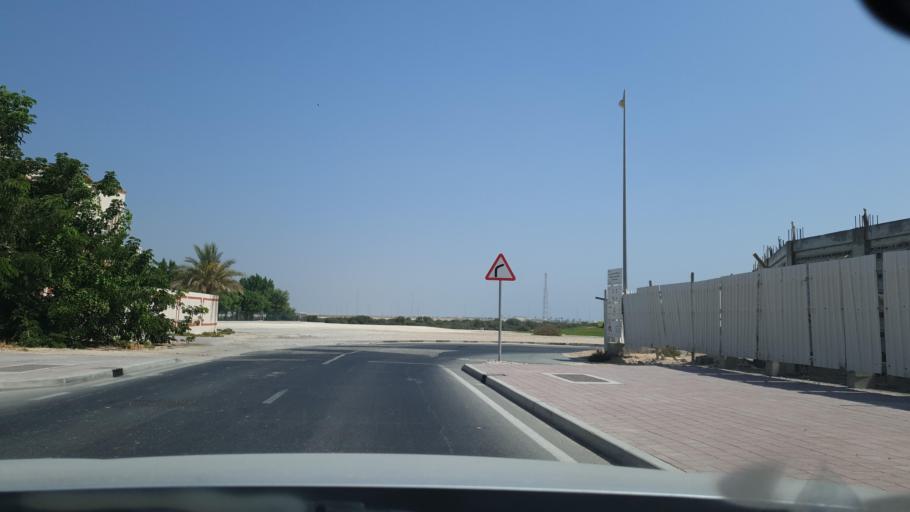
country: QA
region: Al Khawr
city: Al Khawr
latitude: 25.6827
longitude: 51.5249
